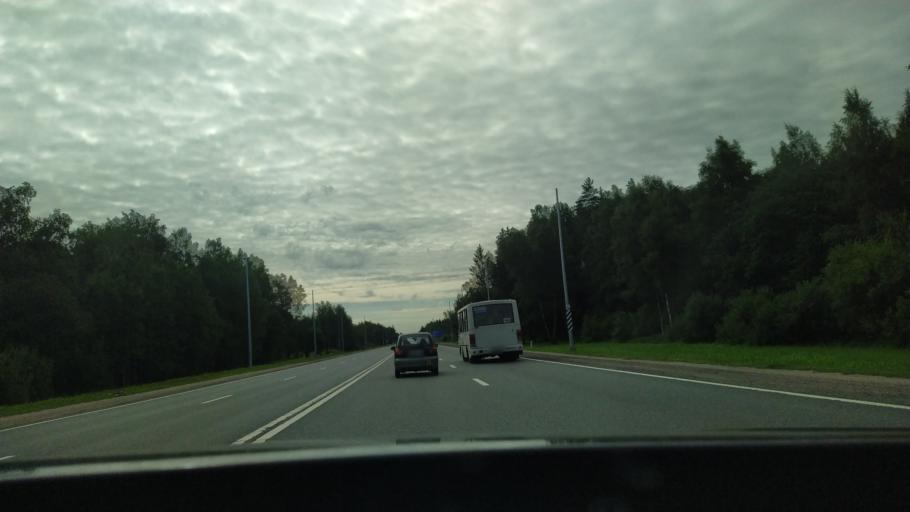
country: RU
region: Leningrad
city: Ul'yanovka
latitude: 59.5886
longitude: 30.7905
